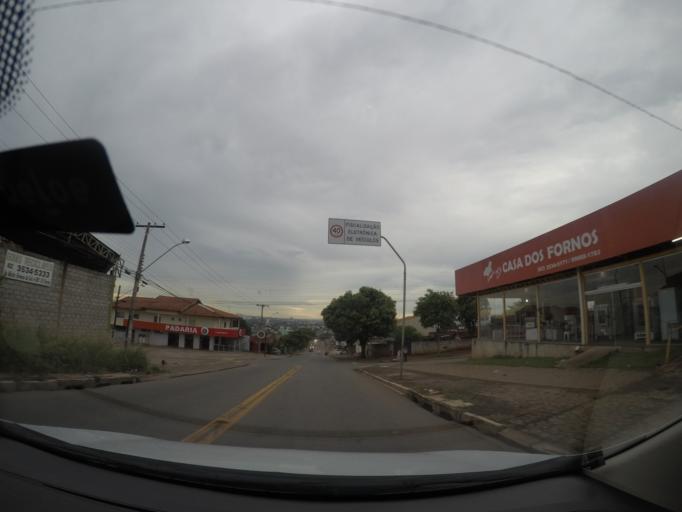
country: BR
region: Goias
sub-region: Goiania
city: Goiania
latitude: -16.6473
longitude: -49.2965
